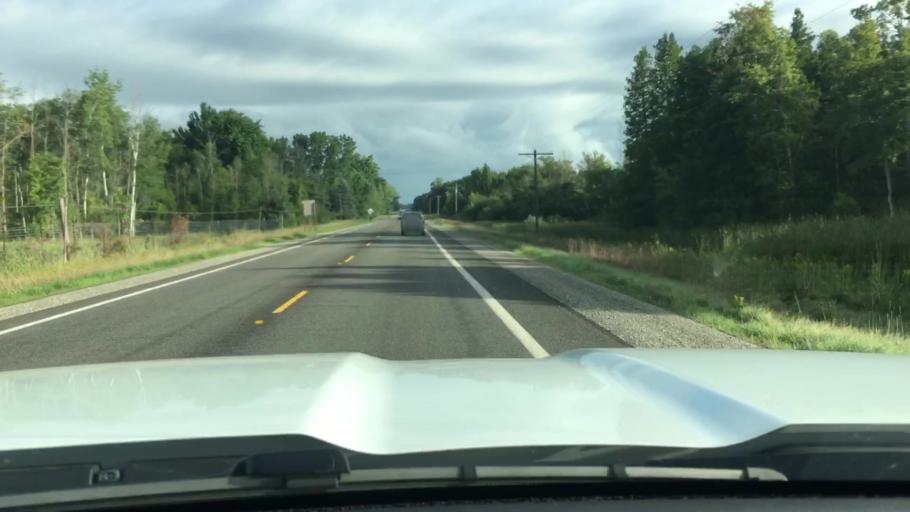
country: US
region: Michigan
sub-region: Tuscola County
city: Caro
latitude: 43.4188
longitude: -83.3843
